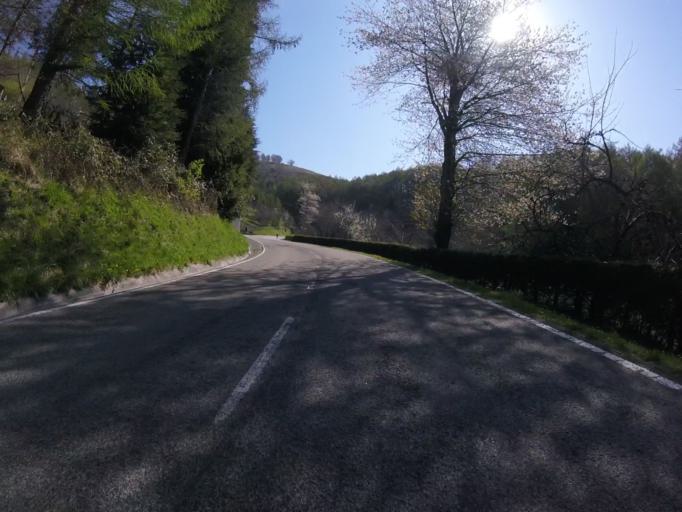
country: ES
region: Navarre
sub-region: Provincia de Navarra
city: Leitza
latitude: 43.0903
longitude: -1.8896
